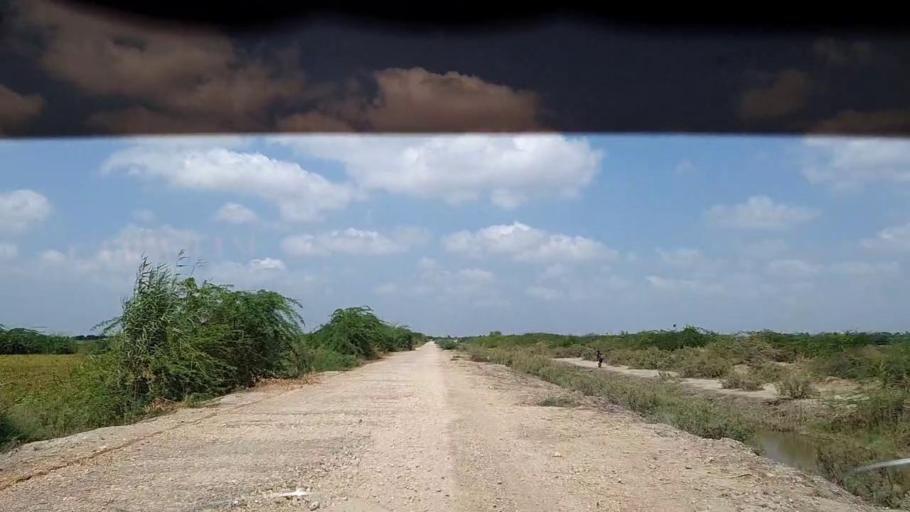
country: PK
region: Sindh
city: Kadhan
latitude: 24.5843
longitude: 68.9703
